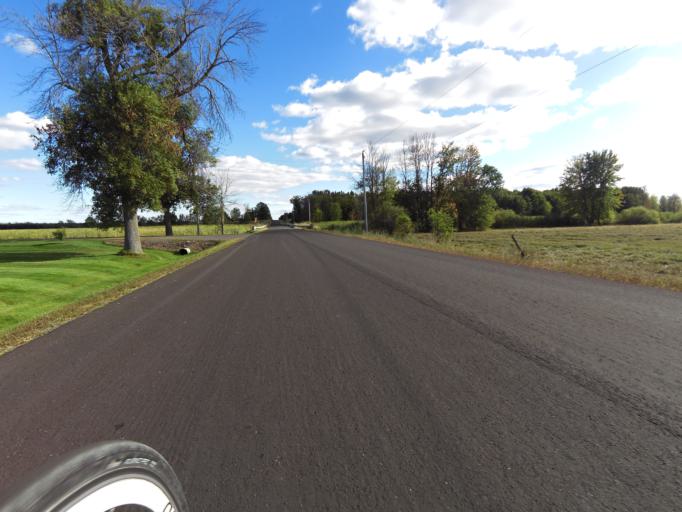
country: CA
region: Ontario
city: Bells Corners
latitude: 45.1199
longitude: -75.6681
